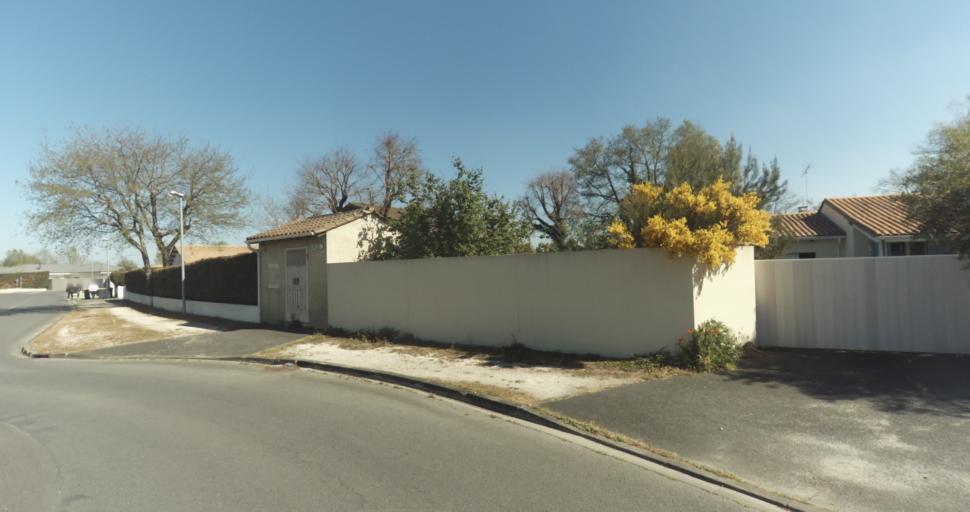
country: FR
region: Aquitaine
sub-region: Departement de la Gironde
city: Martignas-sur-Jalle
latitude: 44.8009
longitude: -0.7824
